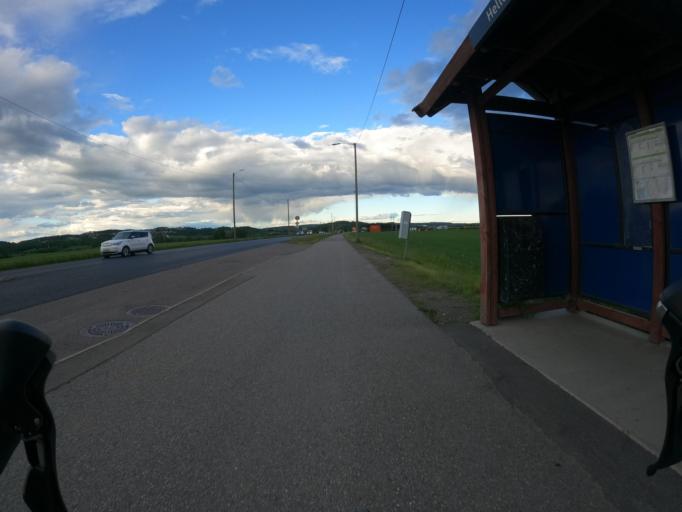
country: NO
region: Akershus
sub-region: Lorenskog
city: Kjenn
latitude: 59.9813
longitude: 10.9802
